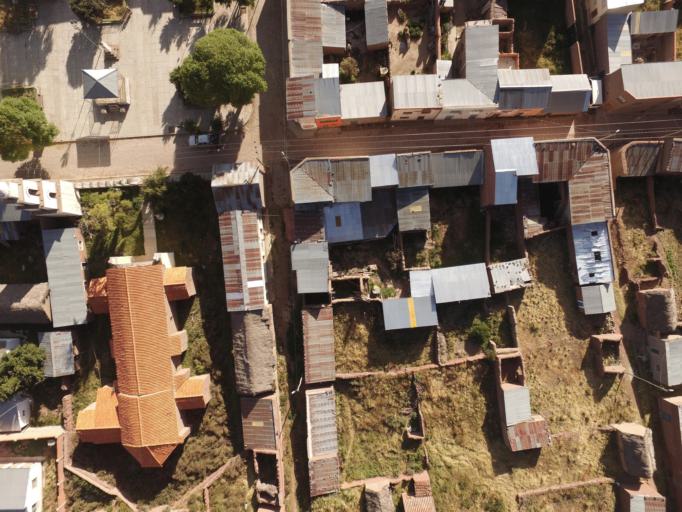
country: BO
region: Oruro
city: Challapata
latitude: -18.6906
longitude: -66.7567
